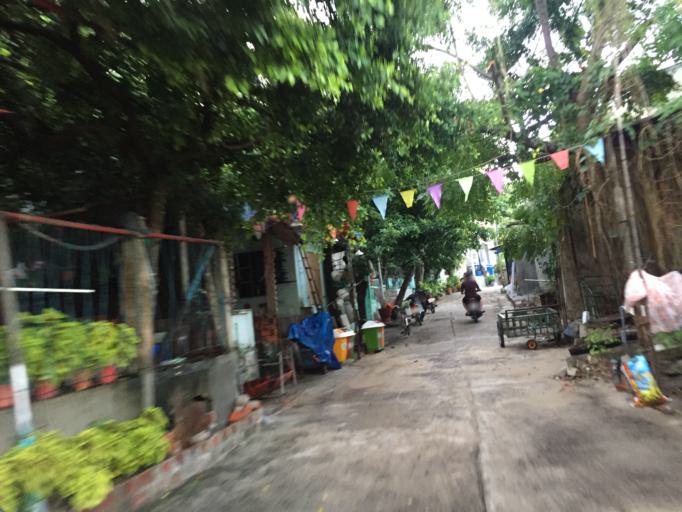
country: VN
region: Quang Nam
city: Hoi An
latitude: 15.9555
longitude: 108.5077
